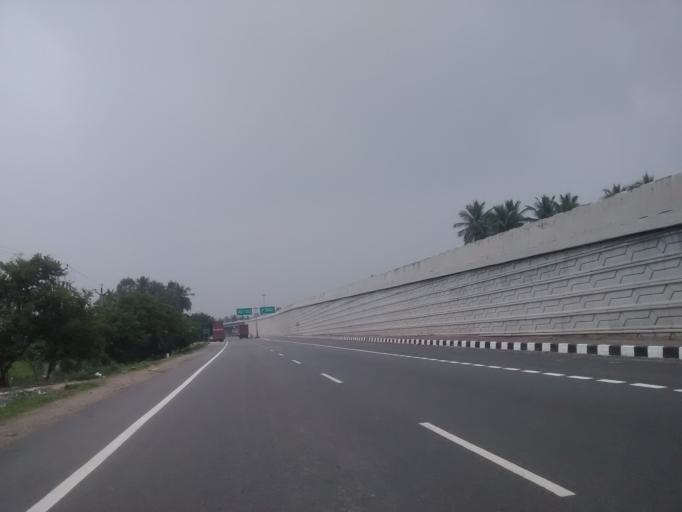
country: IN
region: Tamil Nadu
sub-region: Krishnagiri
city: Kaverippattanam
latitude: 12.4031
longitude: 78.2203
